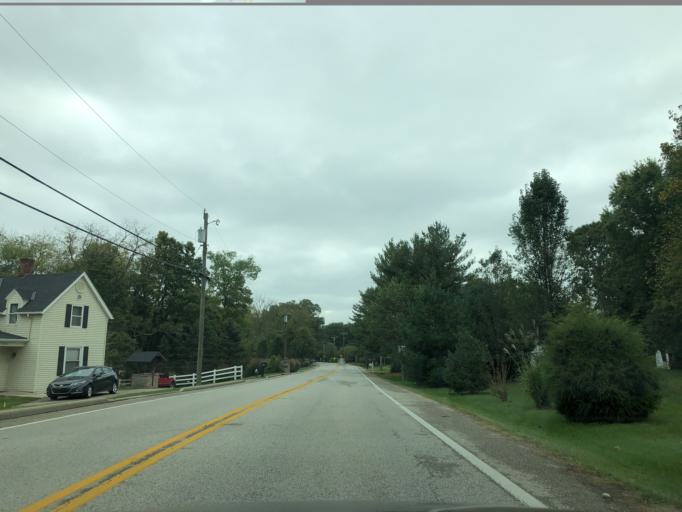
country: US
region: Ohio
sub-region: Hamilton County
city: The Village of Indian Hill
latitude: 39.2627
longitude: -84.3090
